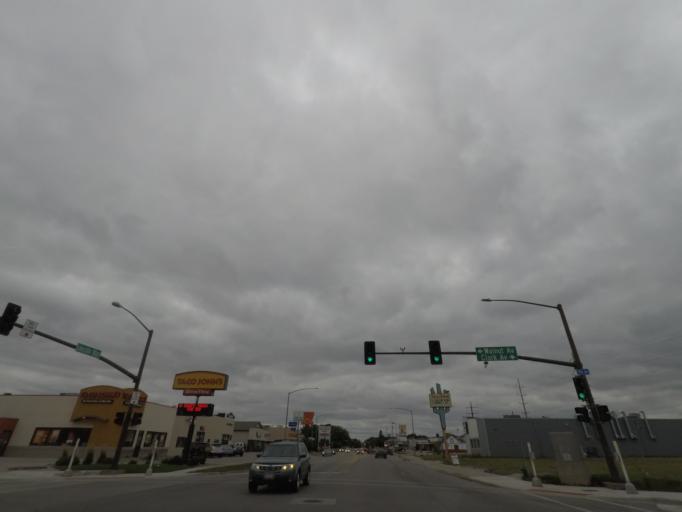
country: US
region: Iowa
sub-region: Story County
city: Ames
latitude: 42.0229
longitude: -93.6168
